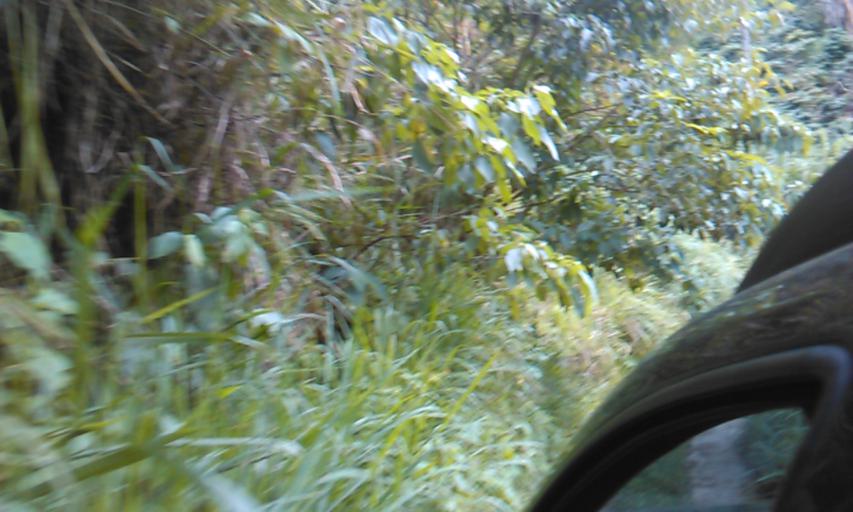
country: CO
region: Quindio
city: Cordoba
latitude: 4.4112
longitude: -75.6822
